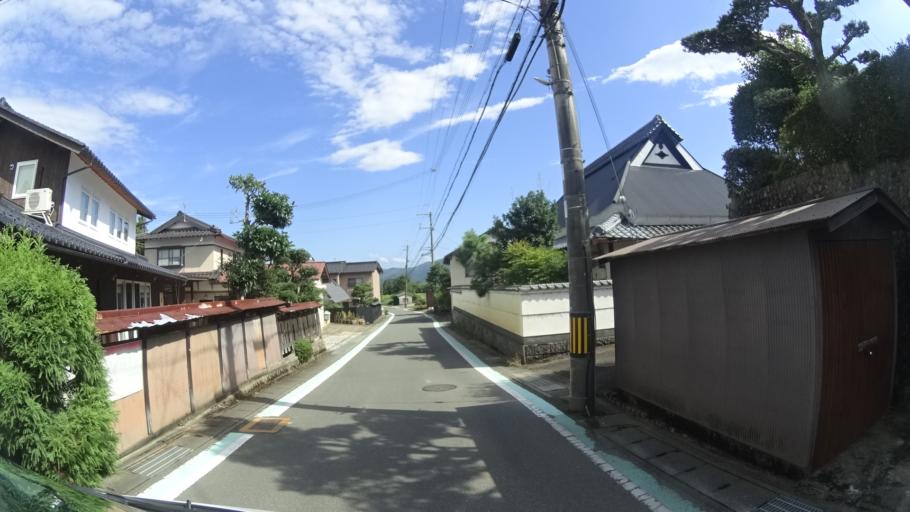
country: JP
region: Kyoto
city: Fukuchiyama
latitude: 35.3250
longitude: 135.1771
